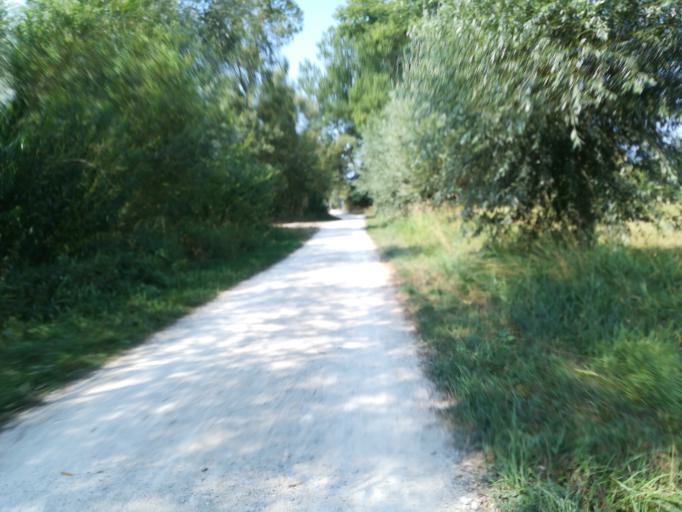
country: DE
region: Baden-Wuerttemberg
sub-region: Freiburg Region
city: Volkertshausen
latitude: 47.7910
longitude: 8.8555
